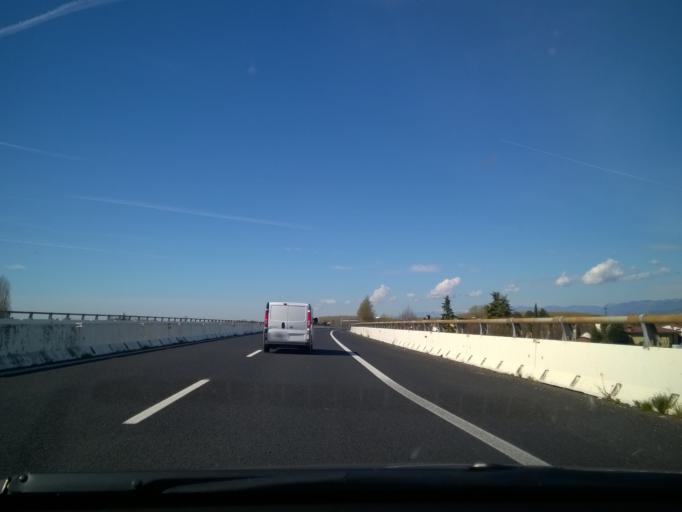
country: IT
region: Friuli Venezia Giulia
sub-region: Provincia di Pordenone
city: Porcia
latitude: 45.9425
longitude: 12.6173
